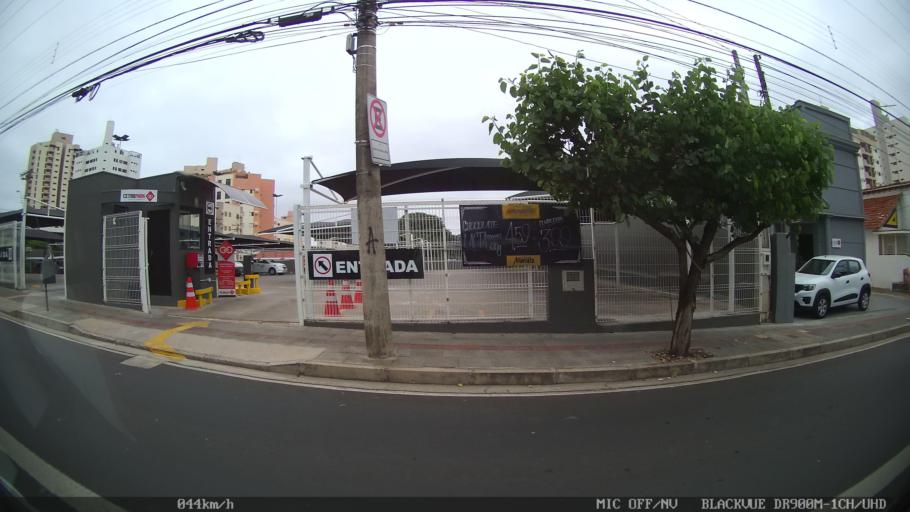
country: BR
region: Sao Paulo
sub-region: Sao Jose Do Rio Preto
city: Sao Jose do Rio Preto
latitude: -20.8179
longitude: -49.3890
